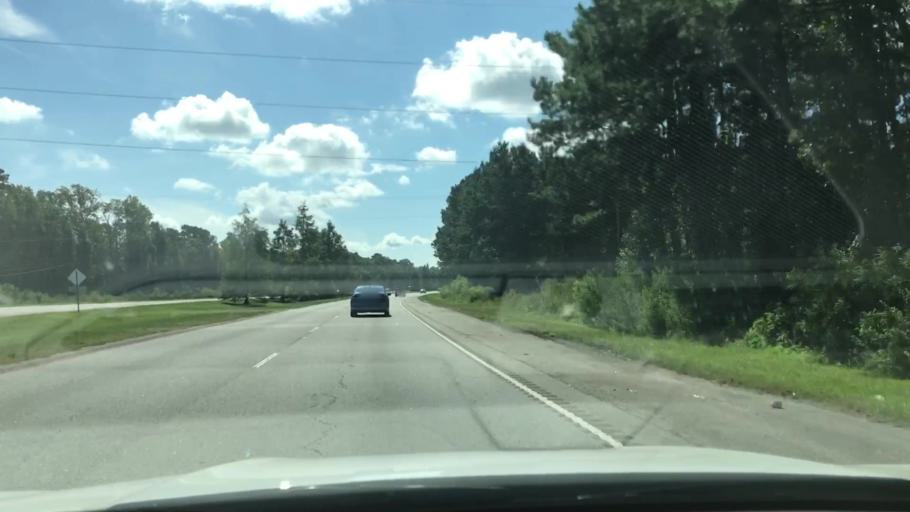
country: US
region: South Carolina
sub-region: Charleston County
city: Shell Point
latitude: 32.8185
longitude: -80.0662
